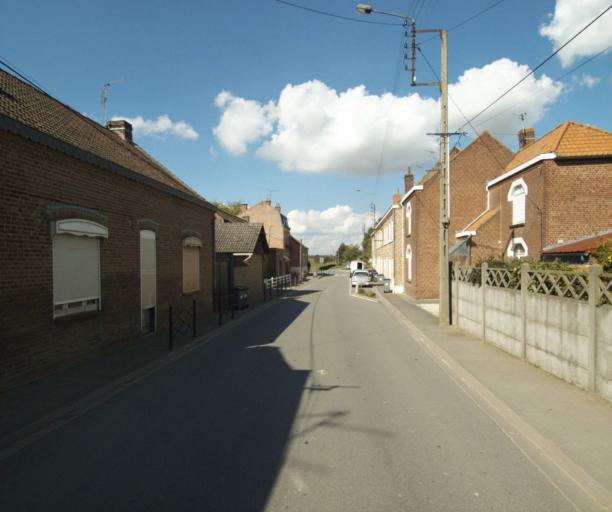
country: FR
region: Nord-Pas-de-Calais
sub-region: Departement du Nord
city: Illies
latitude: 50.5633
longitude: 2.8311
